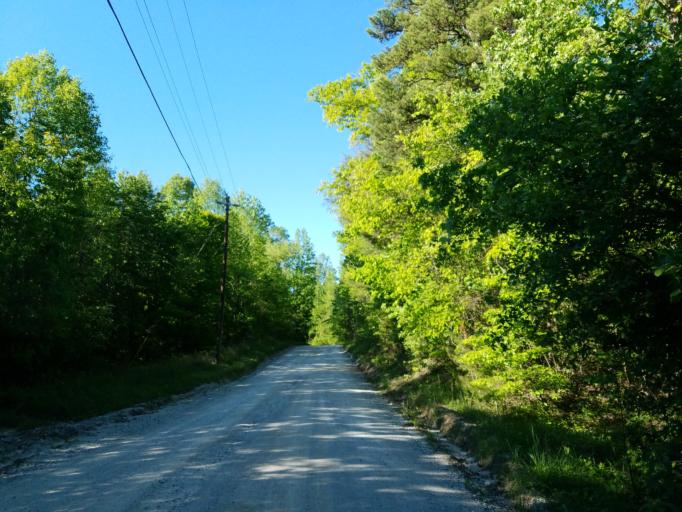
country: US
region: Georgia
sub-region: Gilmer County
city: Ellijay
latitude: 34.6358
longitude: -84.4967
